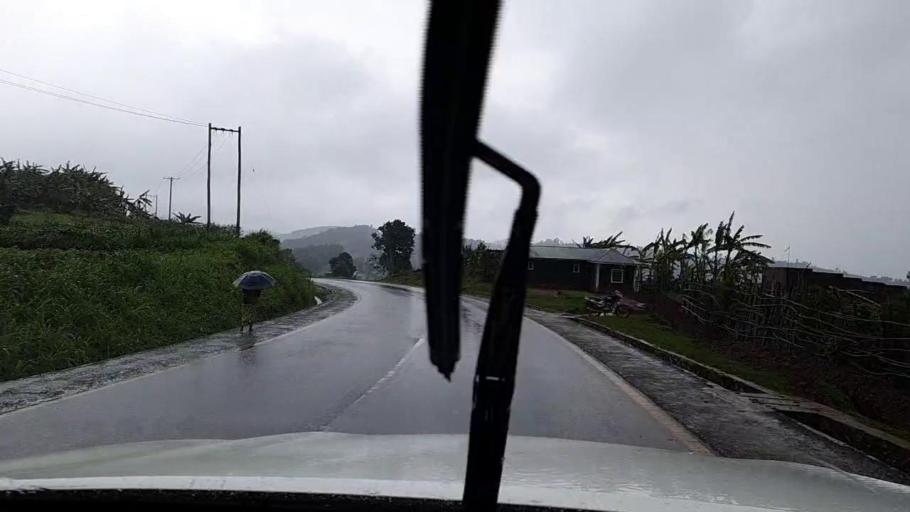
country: RW
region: Western Province
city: Cyangugu
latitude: -2.4623
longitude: 28.9875
